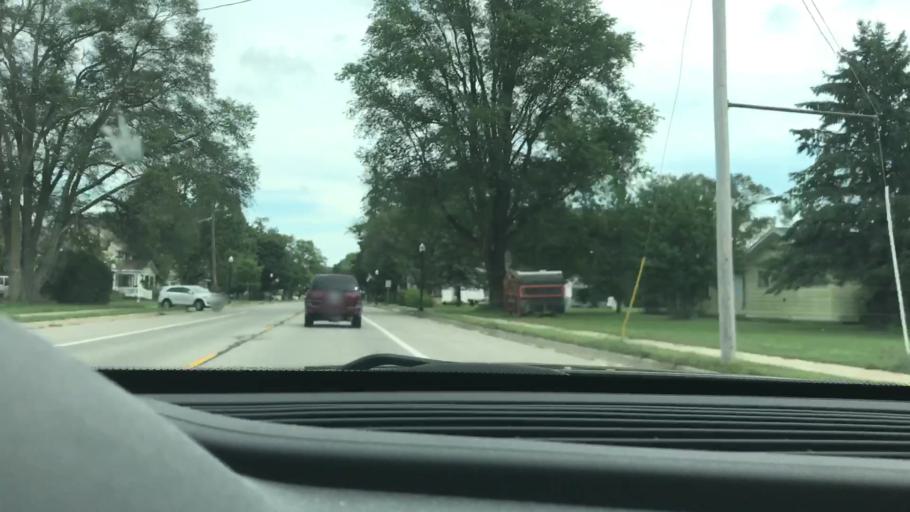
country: US
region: Michigan
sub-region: Antrim County
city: Mancelona
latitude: 44.9024
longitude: -85.0688
